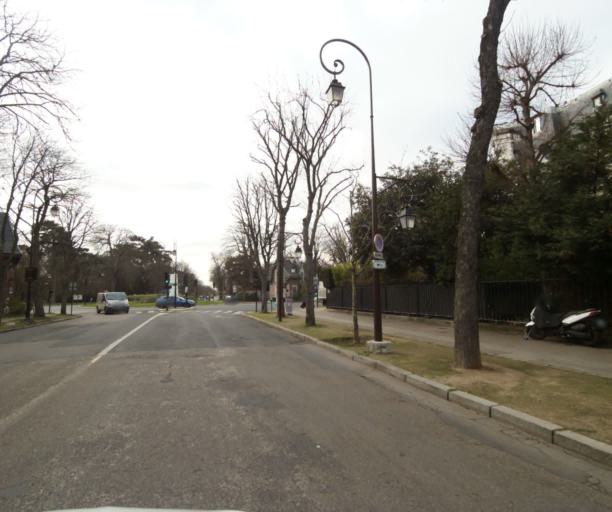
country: FR
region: Ile-de-France
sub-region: Departement des Hauts-de-Seine
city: Neuilly-sur-Seine
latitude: 48.8746
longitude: 2.2554
